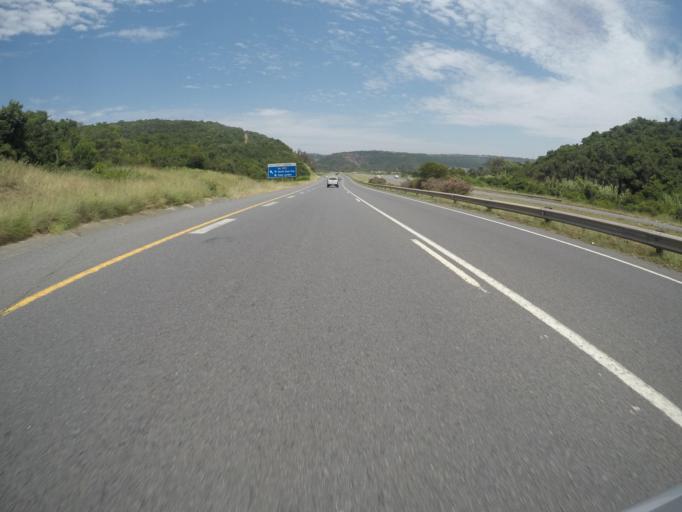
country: ZA
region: Eastern Cape
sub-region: Buffalo City Metropolitan Municipality
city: East London
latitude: -32.9611
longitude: 27.9246
